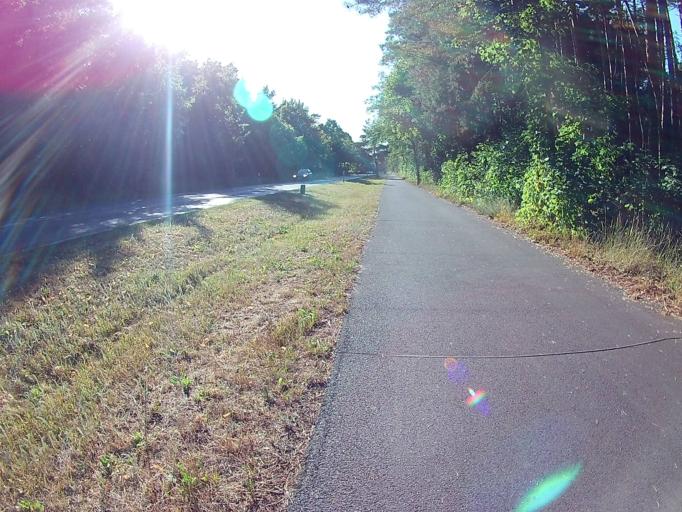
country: DE
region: Brandenburg
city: Zeuthen
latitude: 52.3967
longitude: 13.6096
